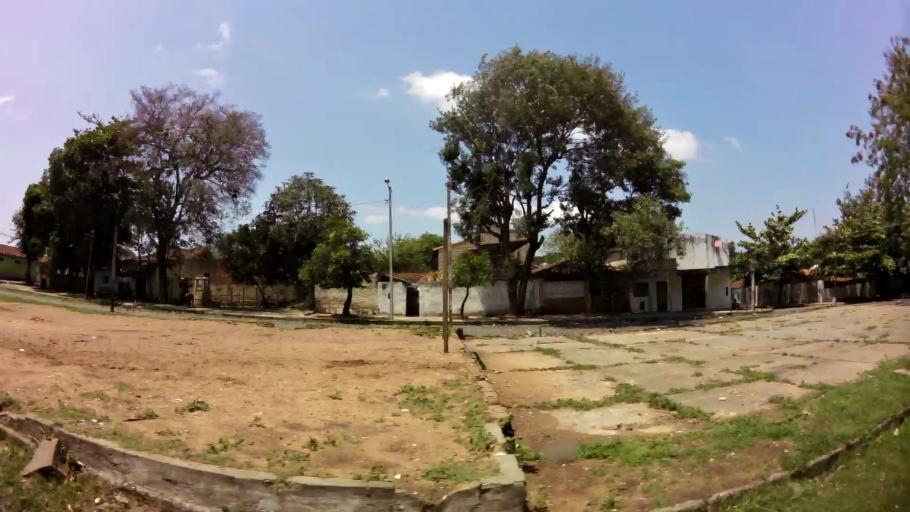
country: PY
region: Asuncion
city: Asuncion
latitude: -25.3126
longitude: -57.6440
